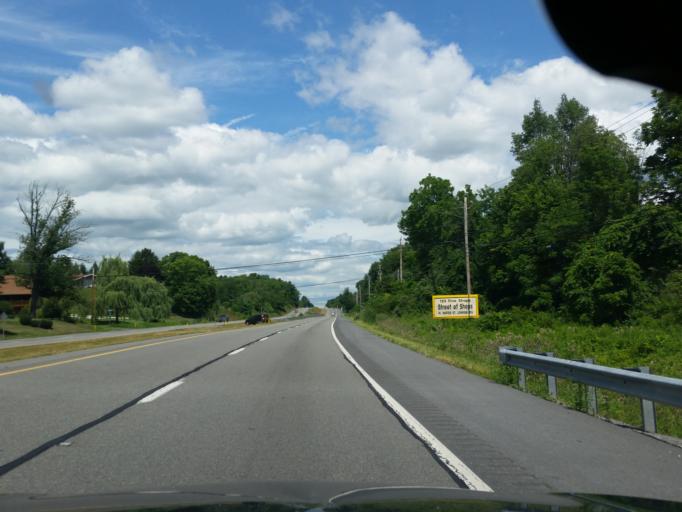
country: US
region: Pennsylvania
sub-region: Union County
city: Lewisburg
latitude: 40.9275
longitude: -76.8664
